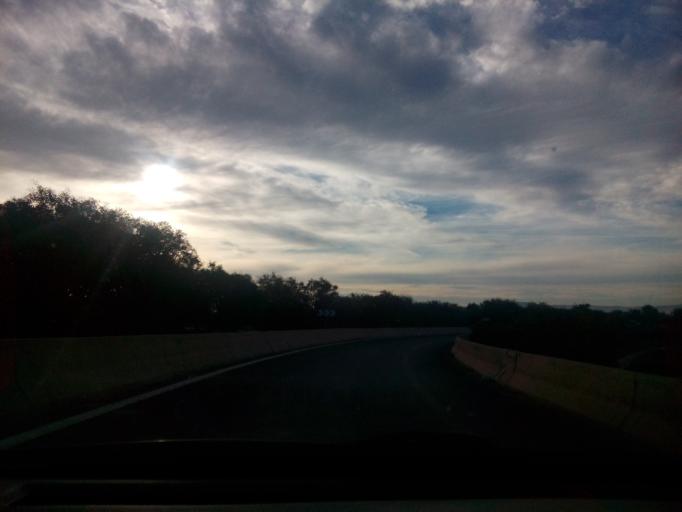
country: DZ
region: Relizane
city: Relizane
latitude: 35.7359
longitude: 0.3090
